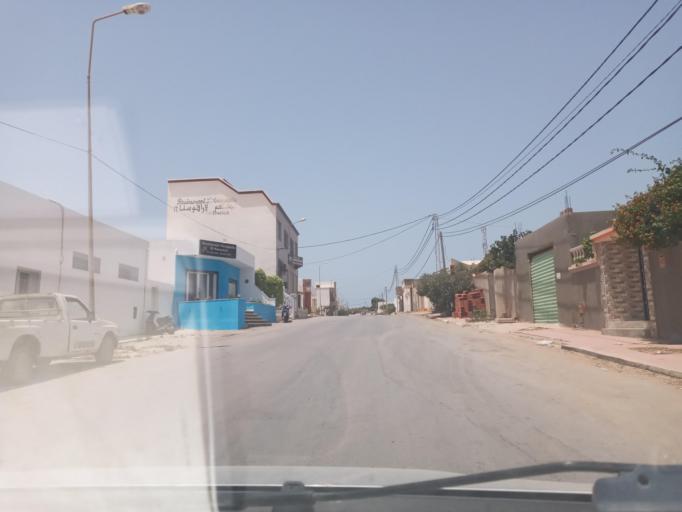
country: TN
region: Nabul
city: El Haouaria
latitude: 37.0541
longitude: 11.0059
